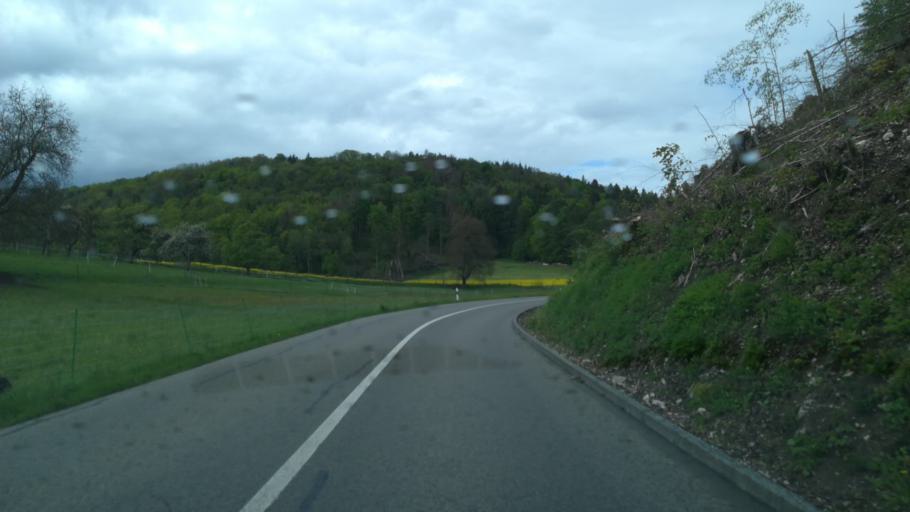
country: CH
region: Schaffhausen
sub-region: Bezirk Reiat
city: Stetten
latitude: 47.7349
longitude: 8.6396
